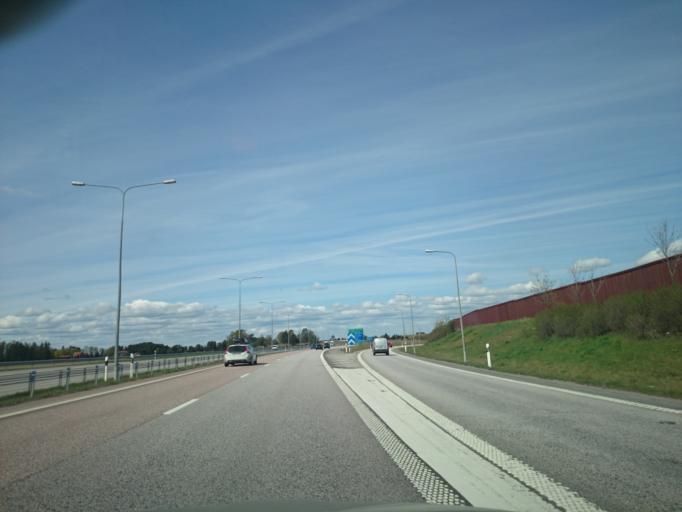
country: SE
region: Uppsala
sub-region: Uppsala Kommun
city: Saevja
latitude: 59.8303
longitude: 17.7367
